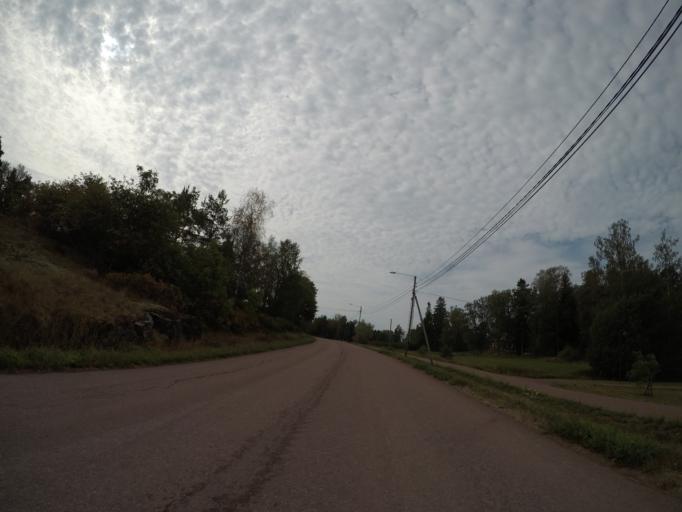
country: AX
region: Alands landsbygd
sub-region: Finstroem
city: Finstroem
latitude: 60.2278
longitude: 19.9854
